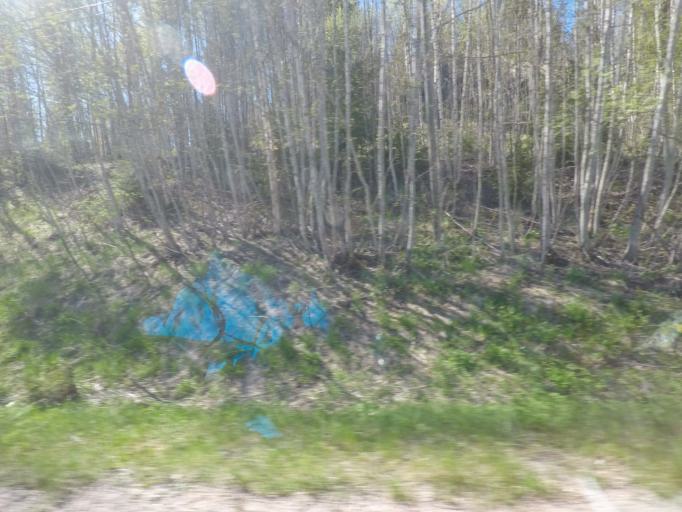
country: FI
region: Uusimaa
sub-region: Helsinki
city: Sammatti
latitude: 60.3734
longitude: 23.8115
